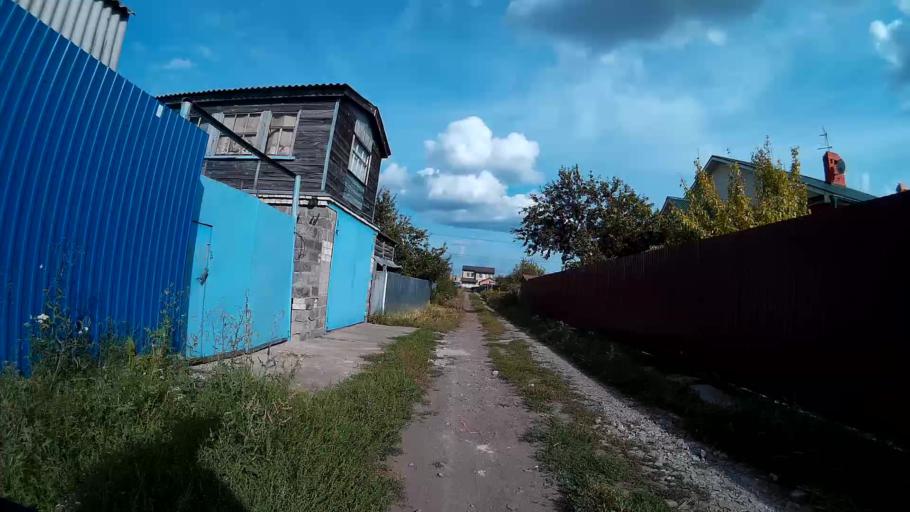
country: RU
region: Ulyanovsk
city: Isheyevka
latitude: 54.2882
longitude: 48.2138
